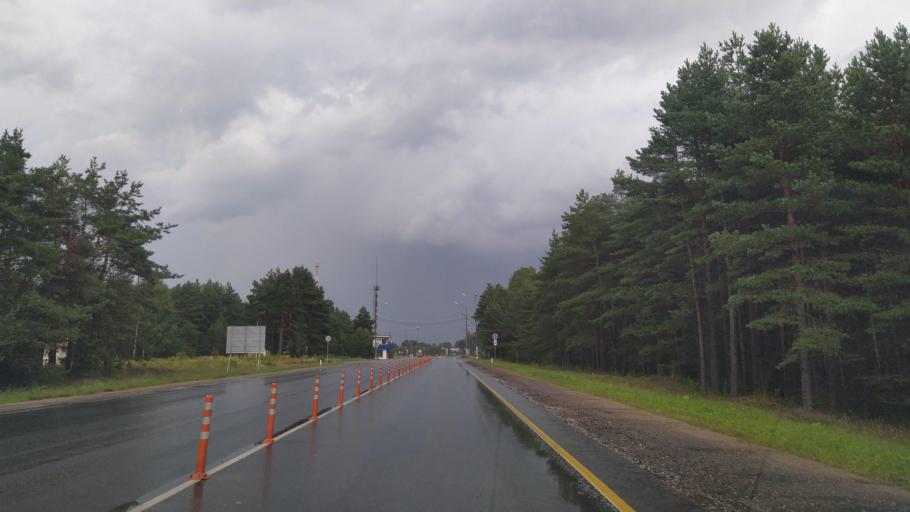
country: RU
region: Pskov
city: Pskov
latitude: 57.7383
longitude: 28.3643
